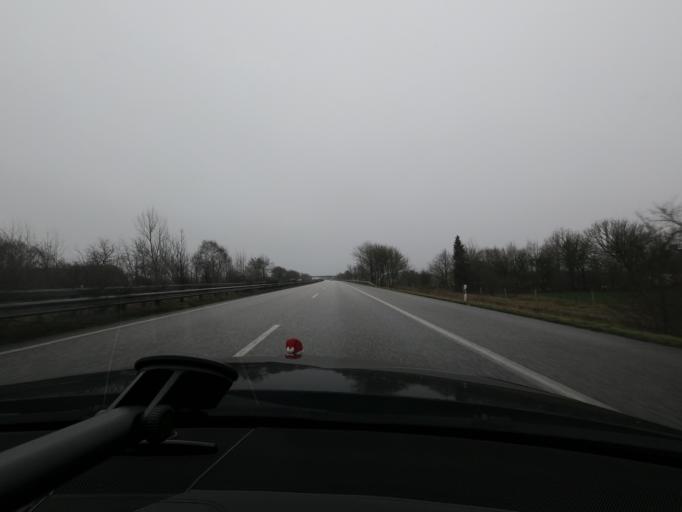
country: DE
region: Schleswig-Holstein
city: Bollingstedt
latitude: 54.6076
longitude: 9.4476
